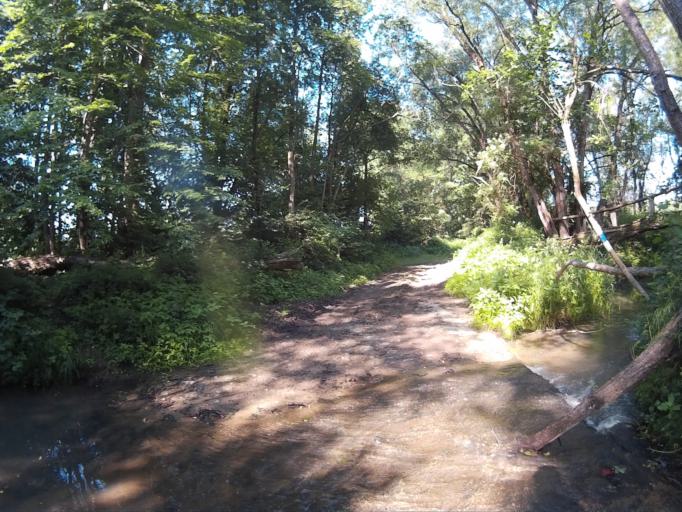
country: AT
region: Burgenland
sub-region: Politischer Bezirk Gussing
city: Heiligenbrunn
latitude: 46.9367
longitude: 16.4699
